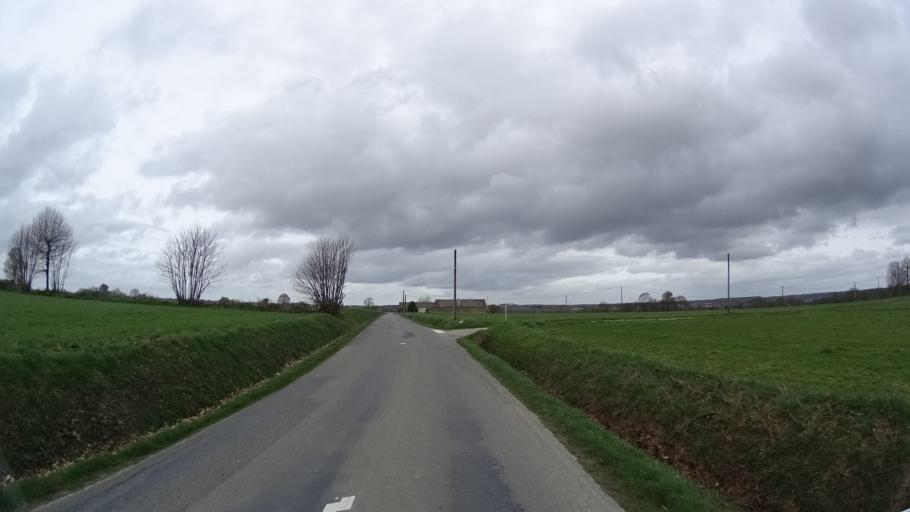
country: FR
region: Brittany
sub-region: Departement d'Ille-et-Vilaine
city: Geveze
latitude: 48.2074
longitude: -1.8277
